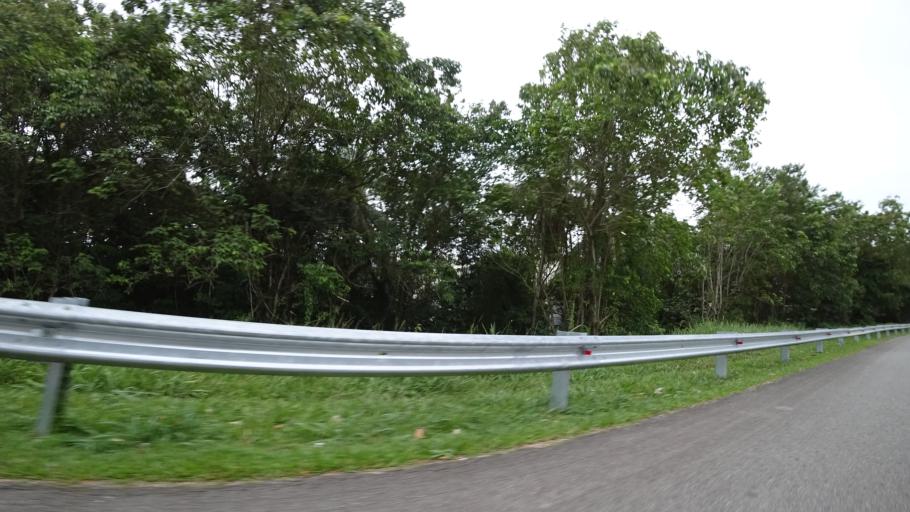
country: BN
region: Brunei and Muara
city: Bandar Seri Begawan
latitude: 4.9298
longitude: 114.9438
